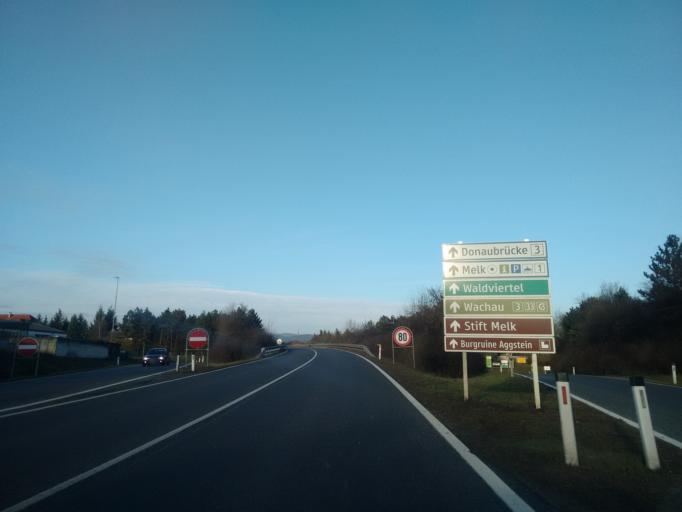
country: AT
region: Lower Austria
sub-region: Politischer Bezirk Melk
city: Melk
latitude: 48.2237
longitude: 15.3501
